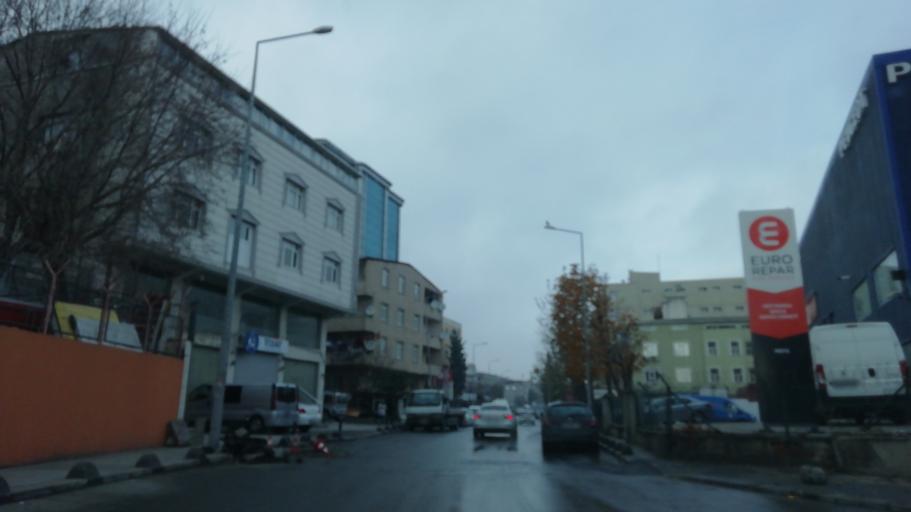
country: TR
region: Istanbul
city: Mahmutbey
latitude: 41.0360
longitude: 28.8067
